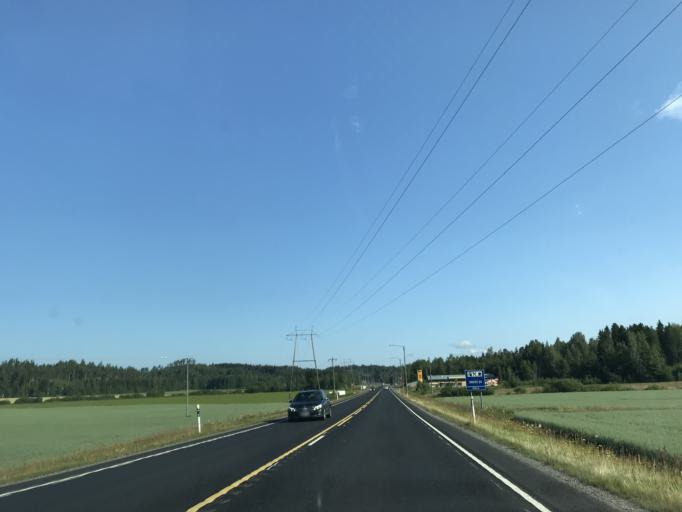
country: FI
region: Paijanne Tavastia
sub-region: Lahti
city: Lahti
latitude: 61.1177
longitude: 25.6412
